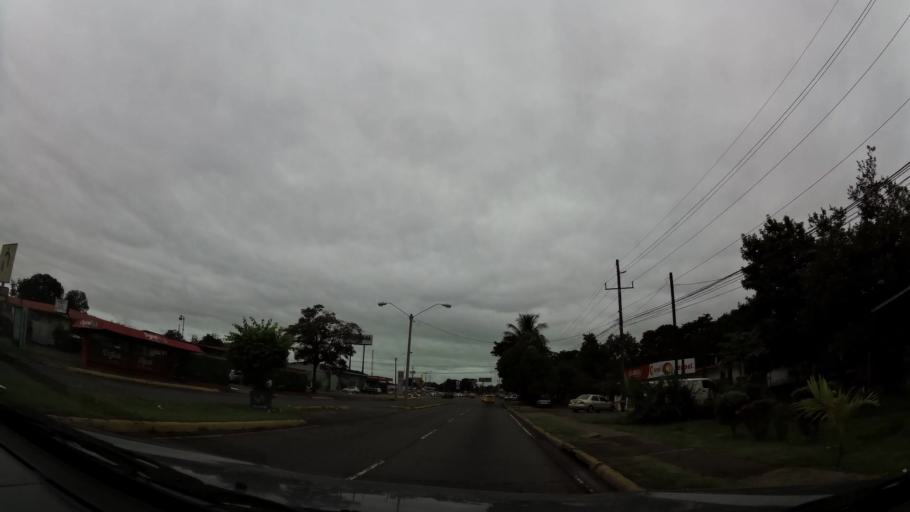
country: PA
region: Chiriqui
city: David
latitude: 8.4326
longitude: -82.4417
